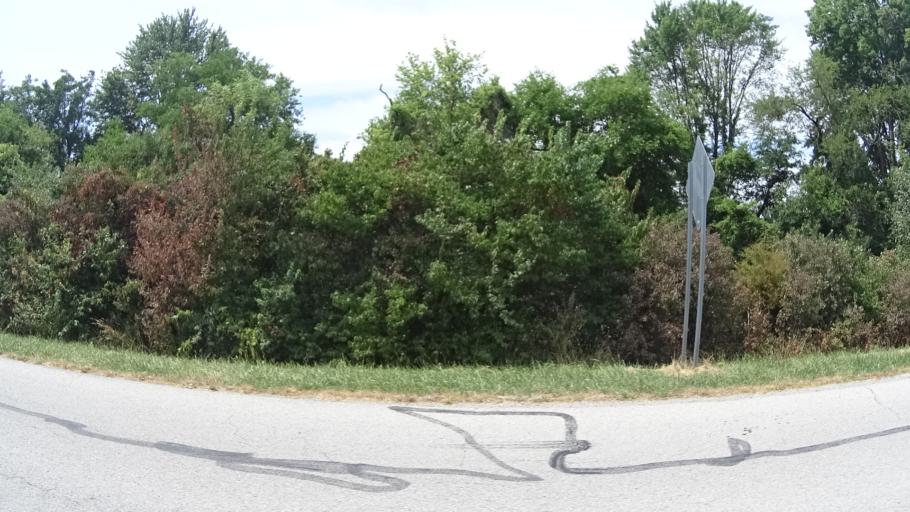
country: US
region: Ohio
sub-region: Erie County
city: Sandusky
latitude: 41.4267
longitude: -82.7710
